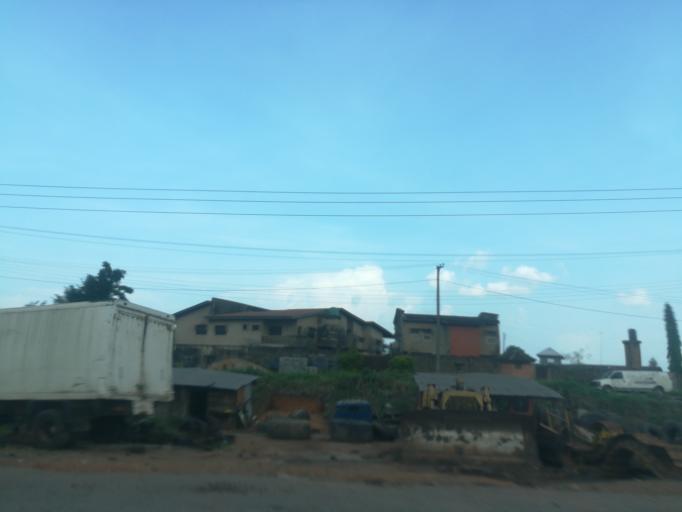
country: NG
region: Oyo
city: Ibadan
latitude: 7.4279
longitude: 3.9348
